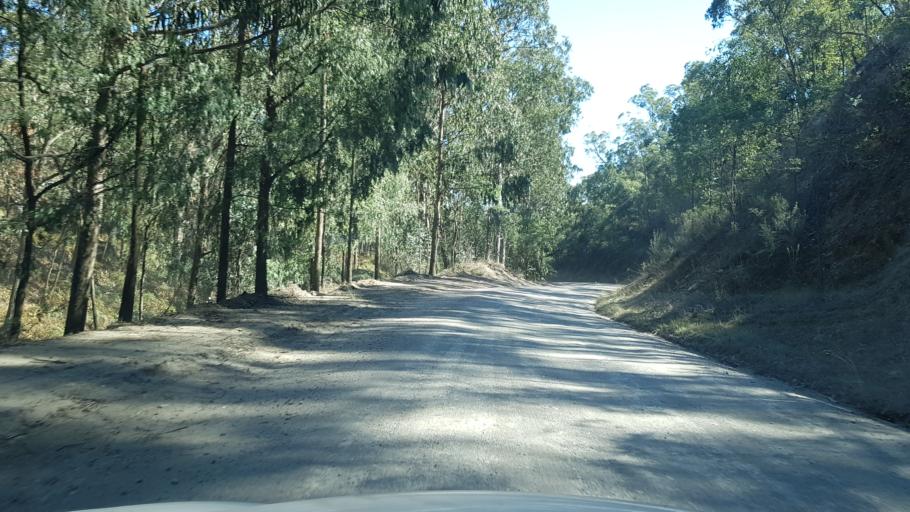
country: AU
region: Victoria
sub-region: Mansfield
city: Mansfield
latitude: -36.8356
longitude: 146.4953
